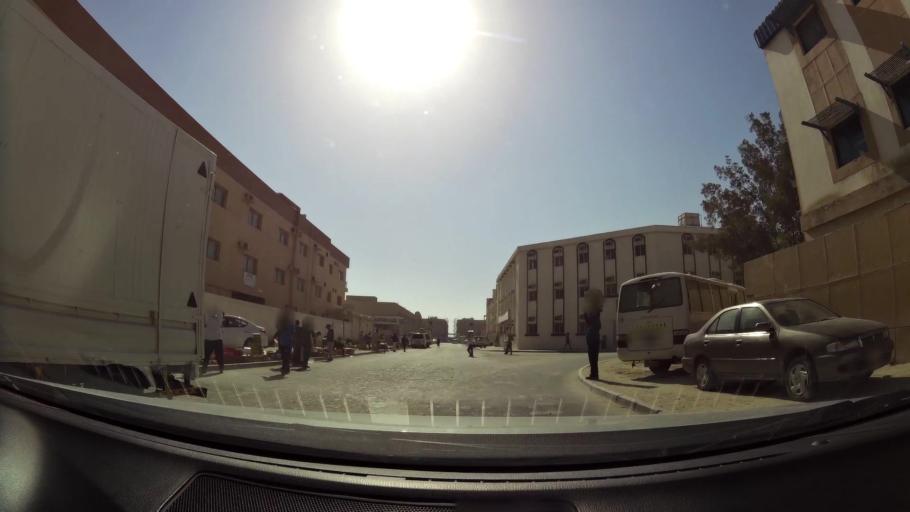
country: AE
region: Dubai
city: Dubai
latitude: 25.0105
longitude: 55.1058
